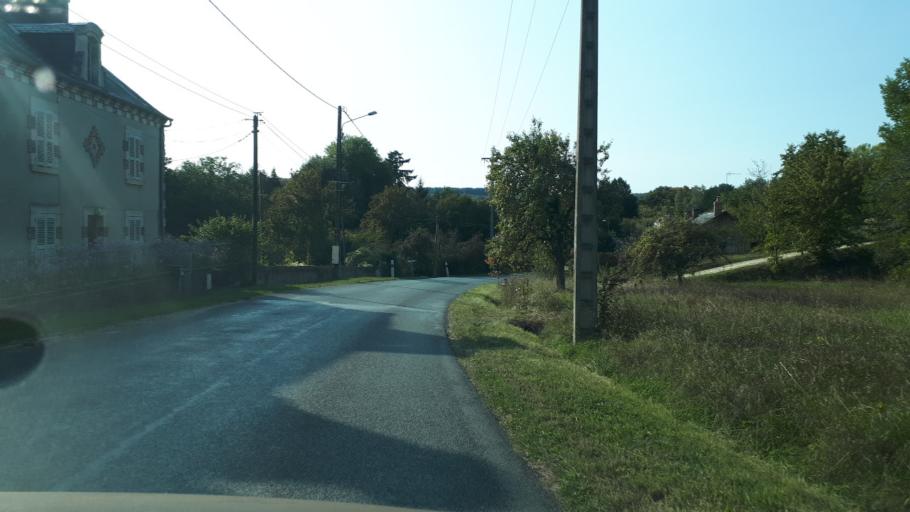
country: FR
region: Centre
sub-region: Departement du Cher
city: Vasselay
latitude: 47.2107
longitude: 2.3929
